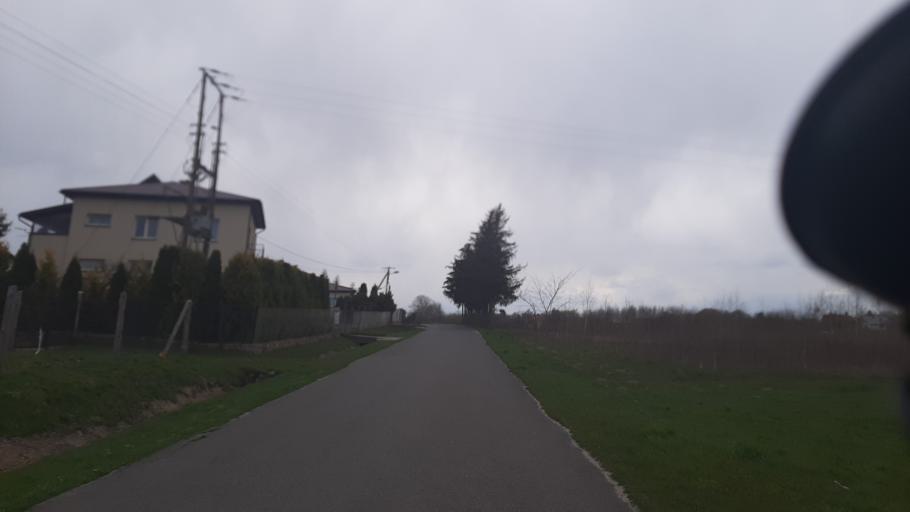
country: PL
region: Lublin Voivodeship
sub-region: Powiat lubelski
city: Niemce
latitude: 51.3637
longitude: 22.5378
